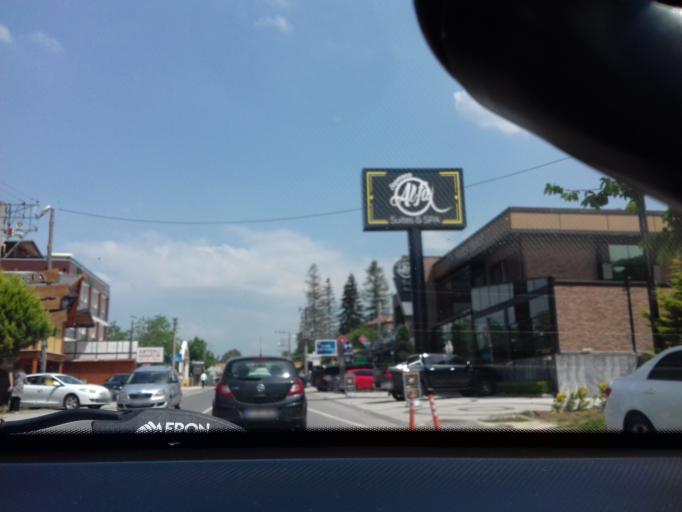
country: TR
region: Sakarya
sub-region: Merkez
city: Sapanca
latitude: 40.6903
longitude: 30.2308
